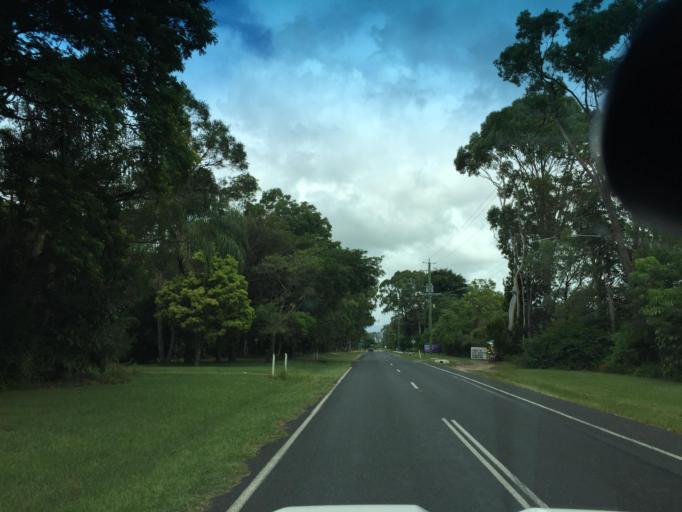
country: AU
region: Queensland
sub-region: Moreton Bay
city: Caboolture
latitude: -27.0563
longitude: 152.9108
